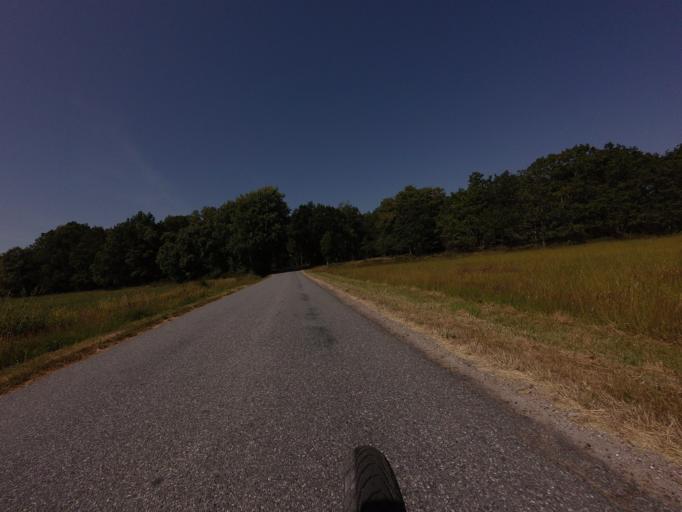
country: DK
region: North Denmark
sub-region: Laeso Kommune
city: Byrum
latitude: 57.2800
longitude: 11.0094
